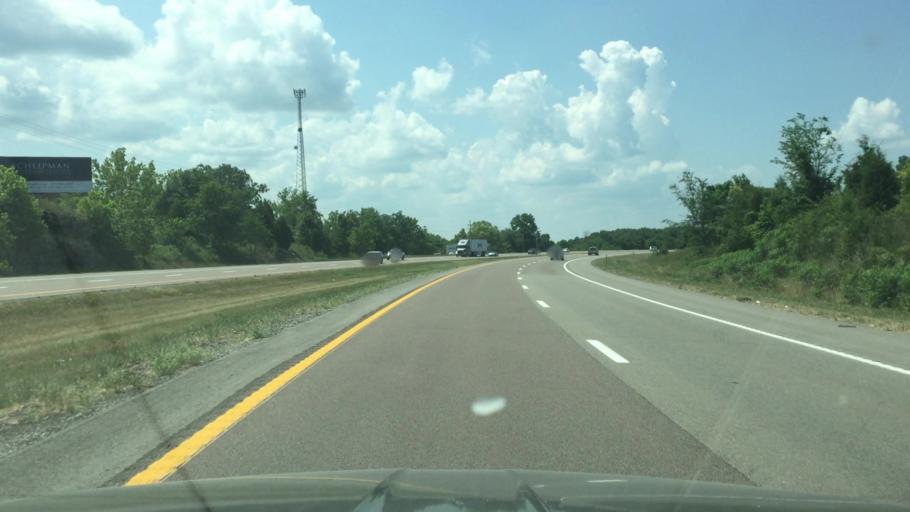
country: US
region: Missouri
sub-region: Miller County
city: Eldon
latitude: 38.2640
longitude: -92.5823
